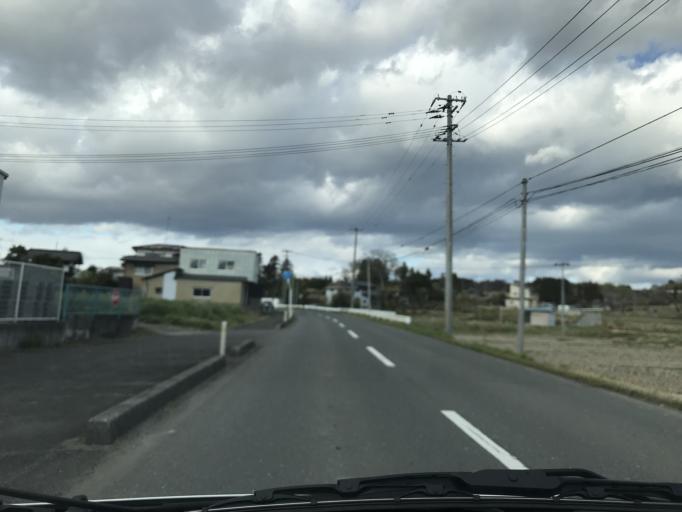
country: JP
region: Miyagi
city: Wakuya
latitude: 38.6326
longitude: 141.2133
